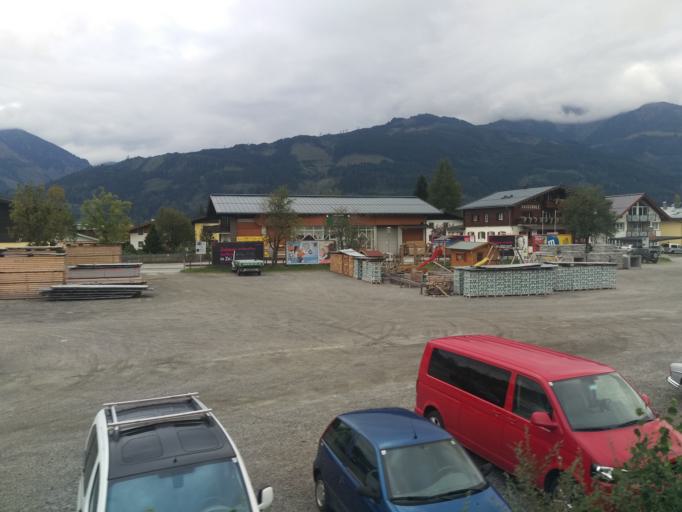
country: AT
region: Salzburg
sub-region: Politischer Bezirk Zell am See
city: Zell am See
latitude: 47.2990
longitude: 12.7891
